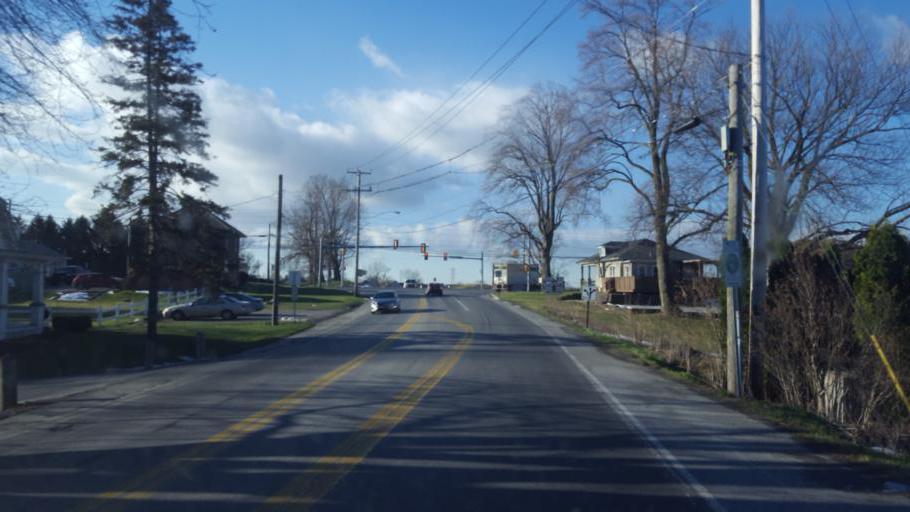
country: US
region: Pennsylvania
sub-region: Lancaster County
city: Lampeter
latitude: 40.0412
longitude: -76.2390
